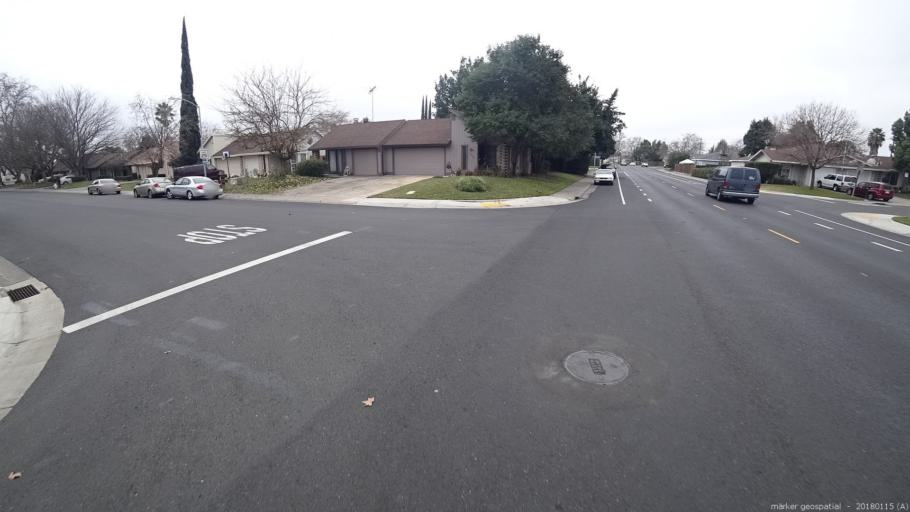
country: US
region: California
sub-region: Sacramento County
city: Rancho Cordova
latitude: 38.5934
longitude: -121.2906
